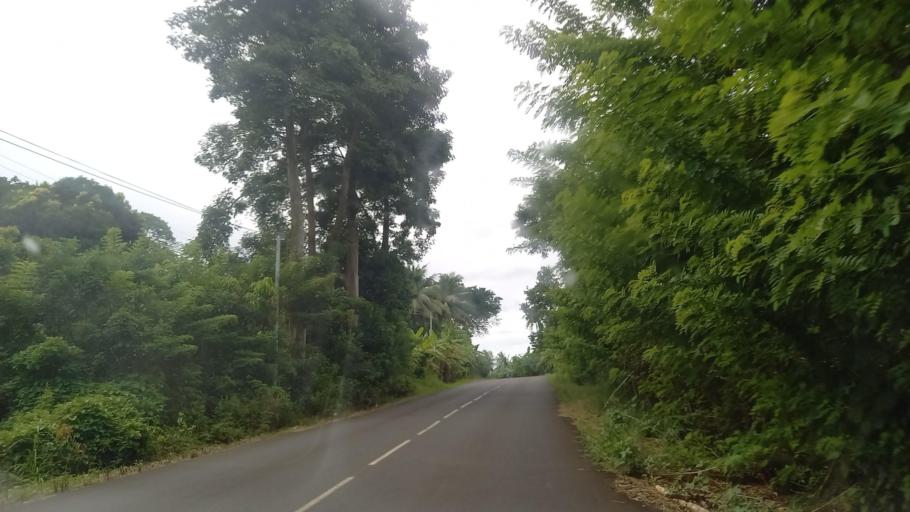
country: YT
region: Boueni
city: Boueni
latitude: -12.9135
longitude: 45.1012
